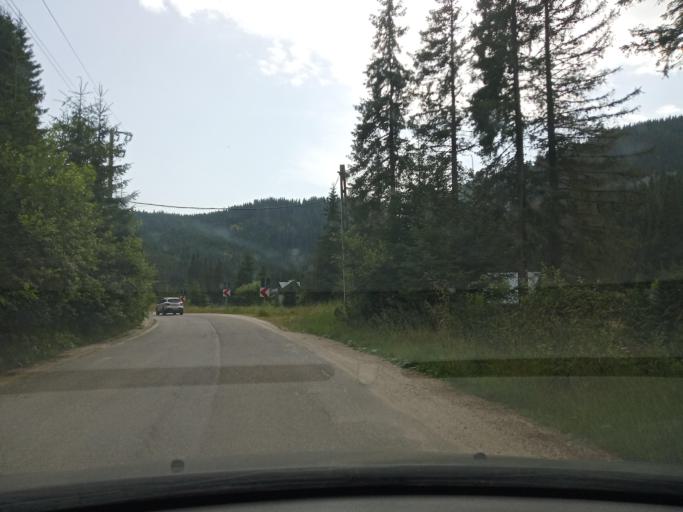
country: RO
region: Dambovita
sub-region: Comuna Moroeni
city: Glod
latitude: 45.3342
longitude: 25.4301
